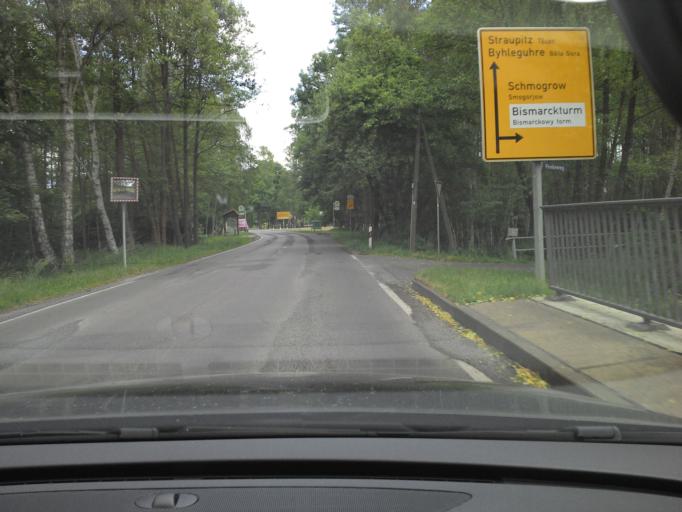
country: DE
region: Brandenburg
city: Burg
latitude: 51.8443
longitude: 14.1542
